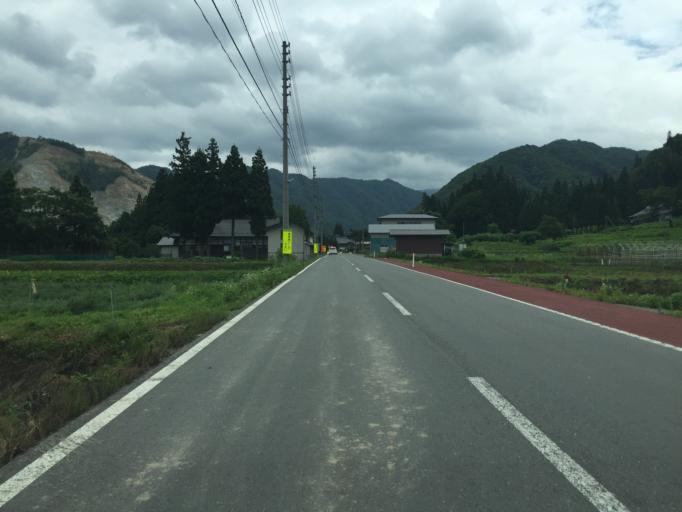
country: JP
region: Yamagata
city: Yonezawa
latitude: 37.8295
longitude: 140.0986
